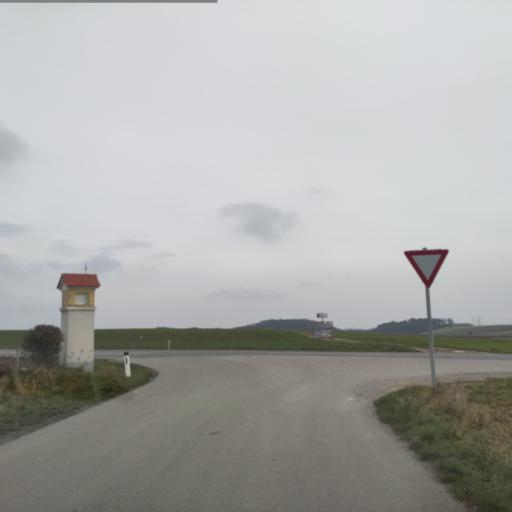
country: AT
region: Lower Austria
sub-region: Politischer Bezirk Sankt Polten
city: Karlstetten
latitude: 48.2463
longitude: 15.5604
